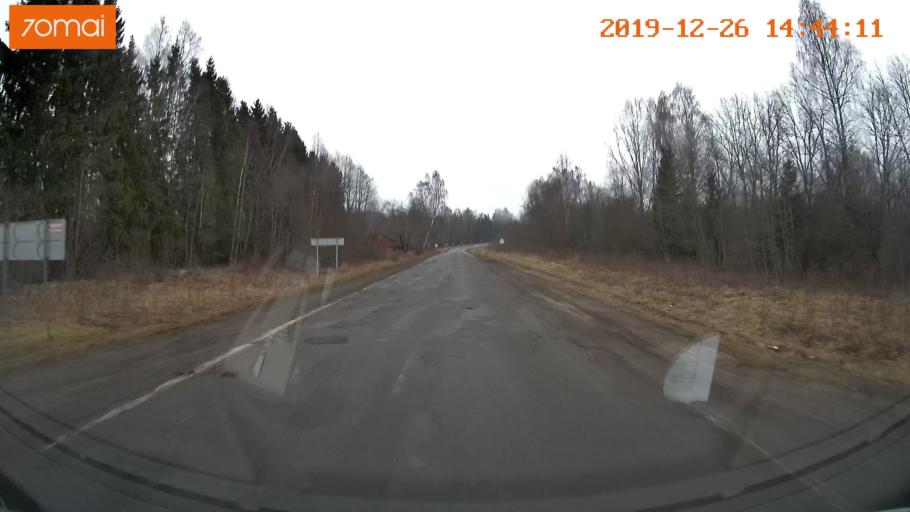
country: RU
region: Jaroslavl
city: Poshekhon'ye
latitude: 58.3503
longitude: 39.0481
